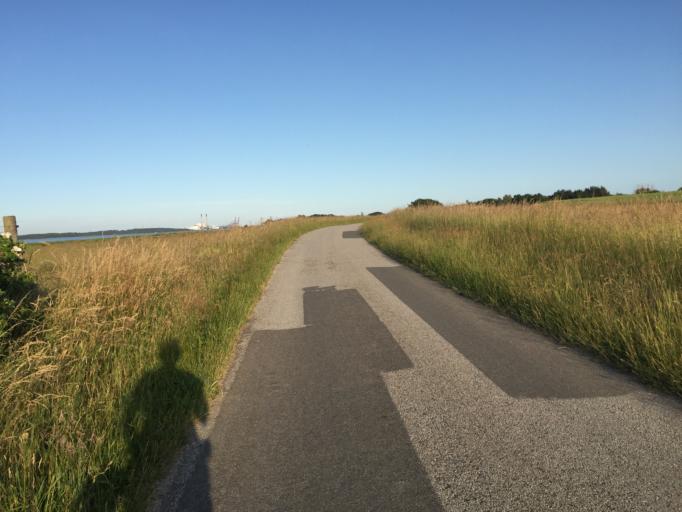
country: DK
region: Zealand
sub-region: Slagelse Kommune
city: Korsor
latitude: 55.2259
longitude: 11.1819
